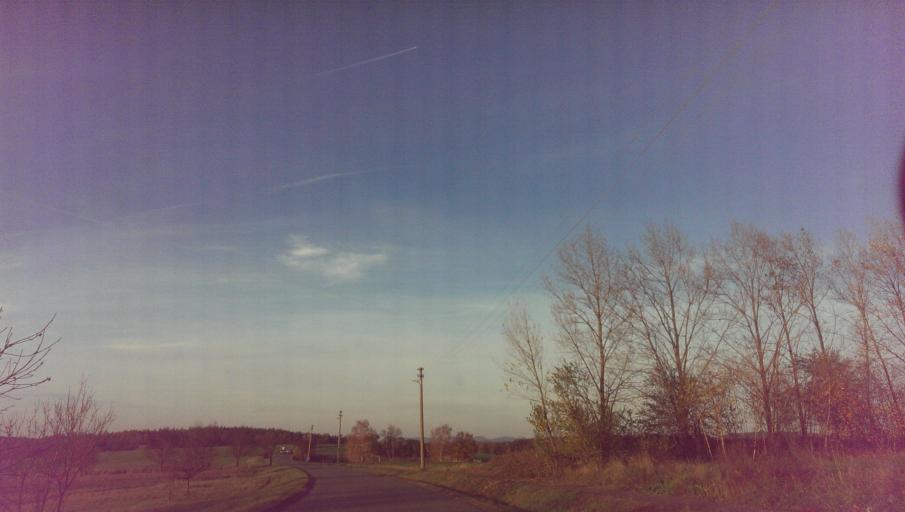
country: CZ
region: Zlin
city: Tecovice
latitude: 49.1730
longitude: 17.6050
